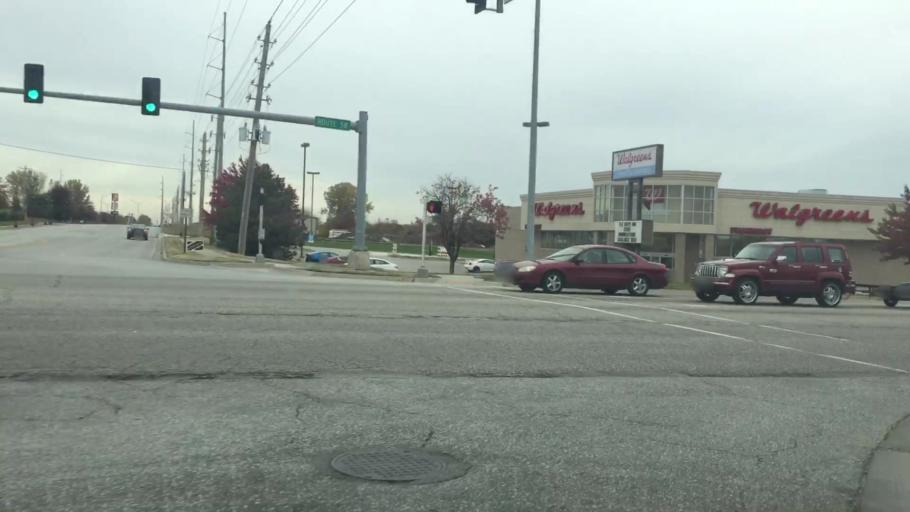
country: US
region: Missouri
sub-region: Cass County
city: Belton
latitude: 38.8134
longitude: -94.5122
